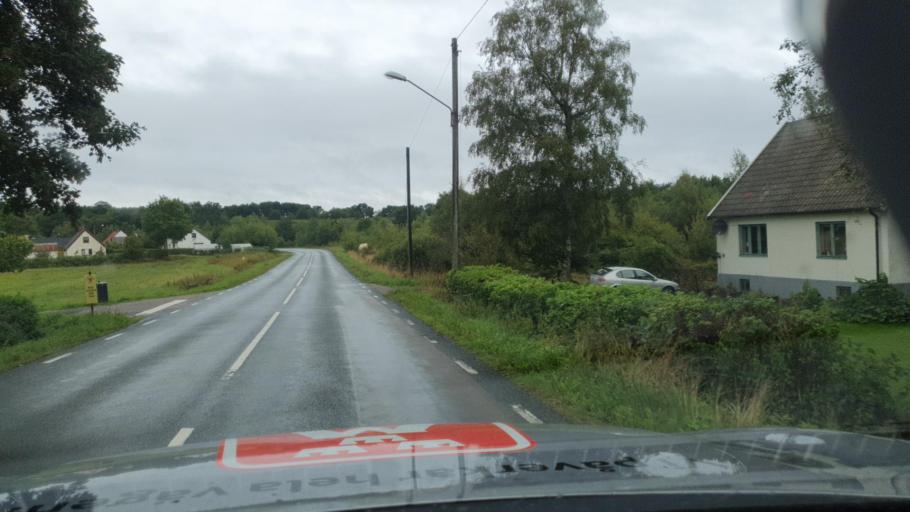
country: SE
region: Skane
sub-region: Simrishamns Kommun
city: Kivik
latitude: 55.5764
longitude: 14.1486
